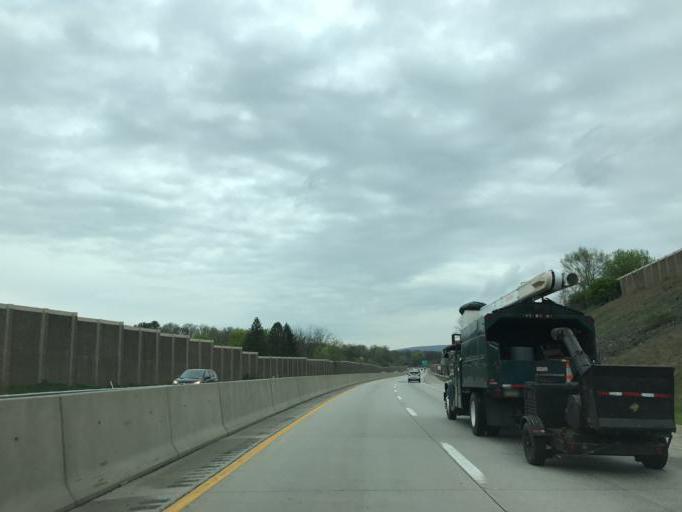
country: US
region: Pennsylvania
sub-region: Berks County
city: West Wyomissing
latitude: 40.3191
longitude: -75.9913
